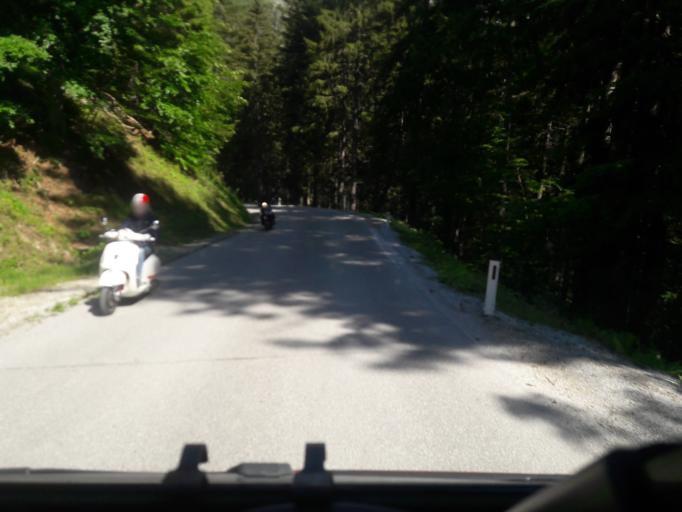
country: AT
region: Styria
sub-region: Politischer Bezirk Liezen
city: Tauplitz
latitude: 47.5777
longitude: 13.9647
